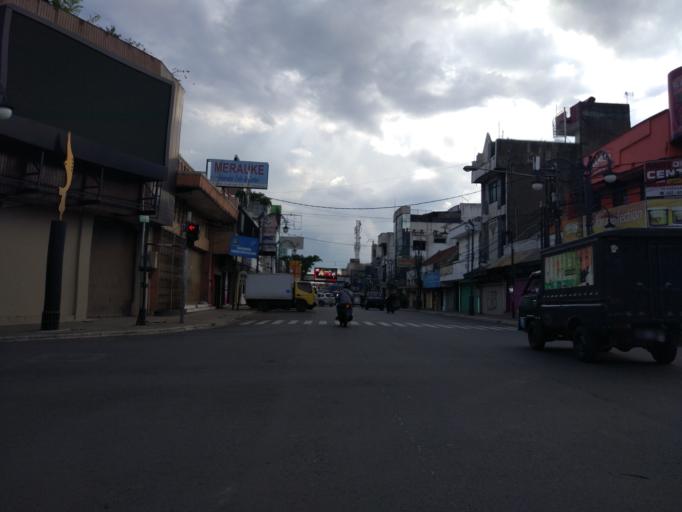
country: ID
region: West Java
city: Bandung
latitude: -6.9202
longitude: 107.5985
